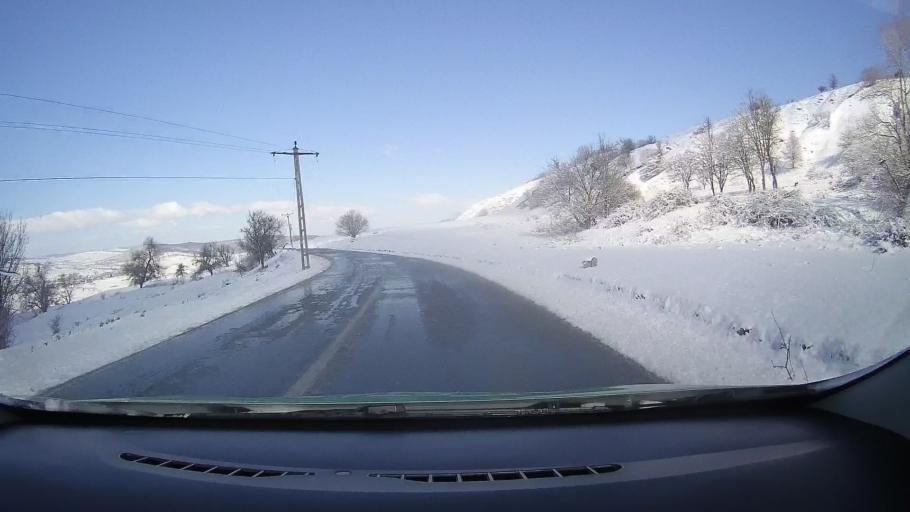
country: RO
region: Sibiu
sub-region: Comuna Rosia
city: Rosia
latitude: 45.7835
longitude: 24.3746
